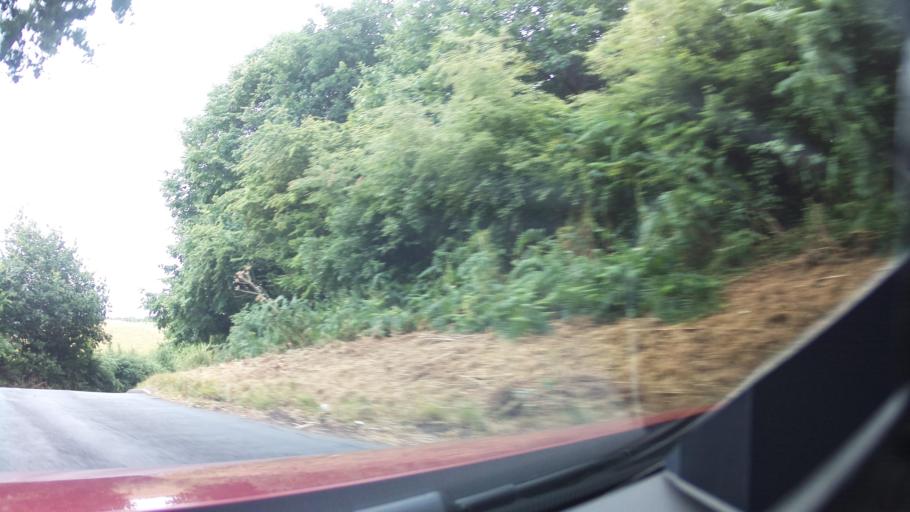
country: GB
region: England
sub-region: Derbyshire
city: Swadlincote
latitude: 52.8025
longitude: -1.5381
